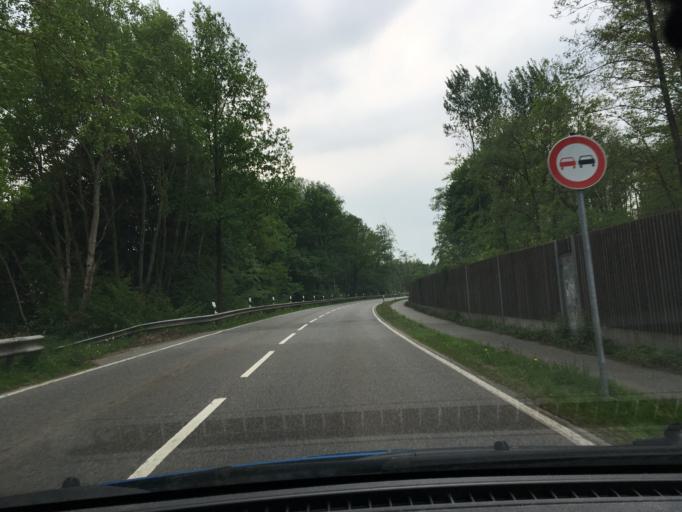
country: DE
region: Lower Saxony
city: Seevetal
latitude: 53.3831
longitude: 9.9958
